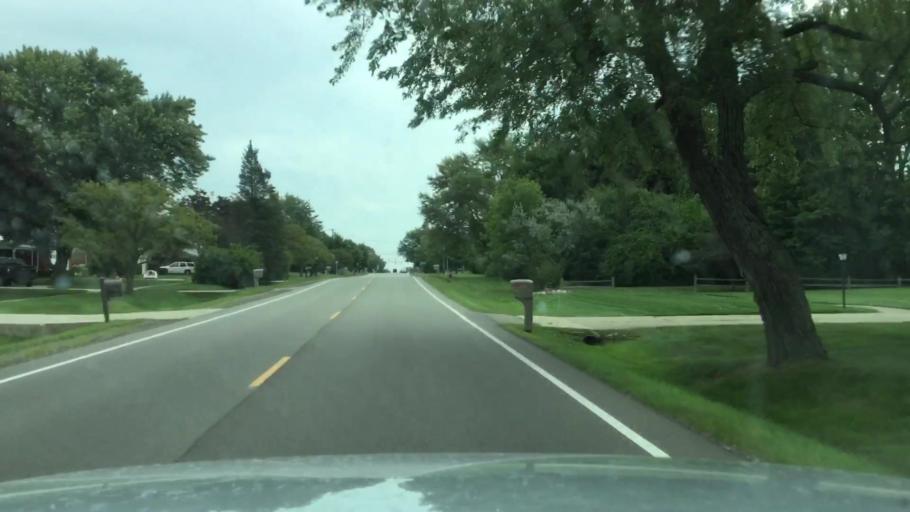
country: US
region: Michigan
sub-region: Oakland County
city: Birmingham
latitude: 42.5761
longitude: -83.1931
